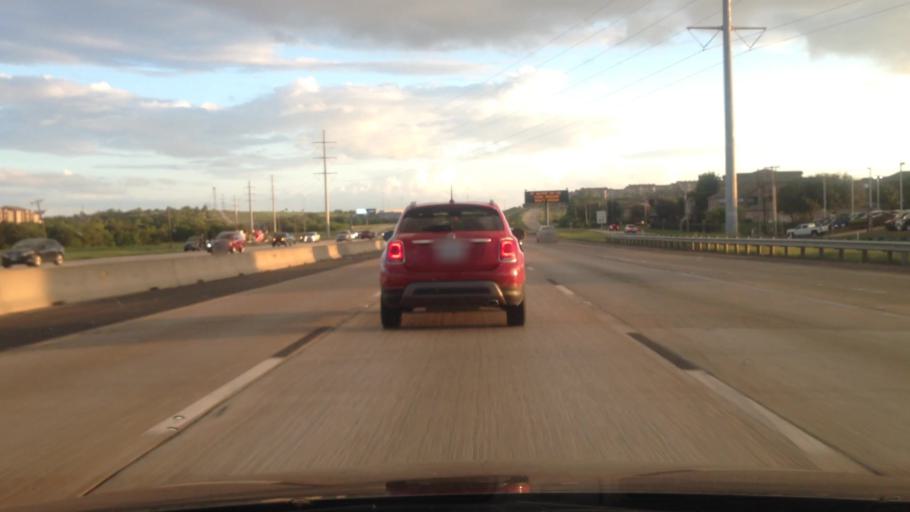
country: US
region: Texas
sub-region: Tarrant County
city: White Settlement
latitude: 32.7560
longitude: -97.4789
